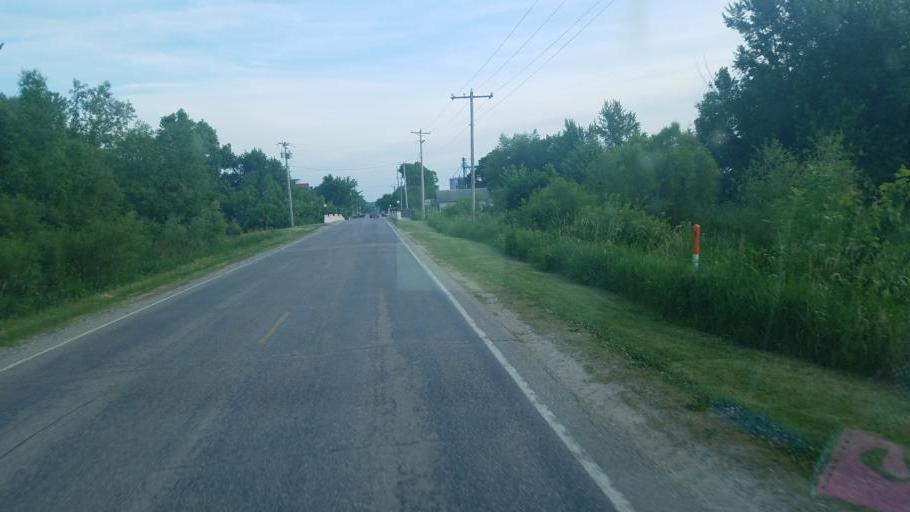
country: US
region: Iowa
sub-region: Benton County
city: Belle Plaine
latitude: 41.9228
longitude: -92.3946
